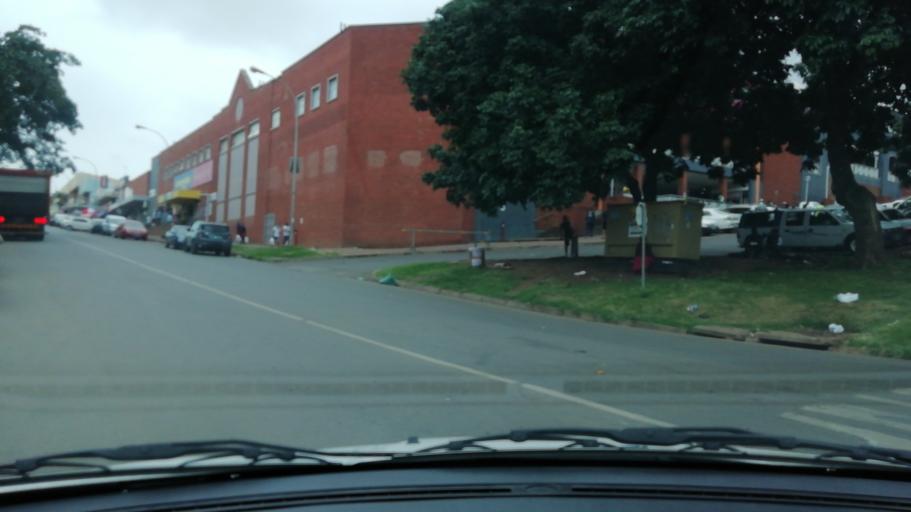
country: ZA
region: KwaZulu-Natal
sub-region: uThungulu District Municipality
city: Empangeni
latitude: -28.7433
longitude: 31.8866
